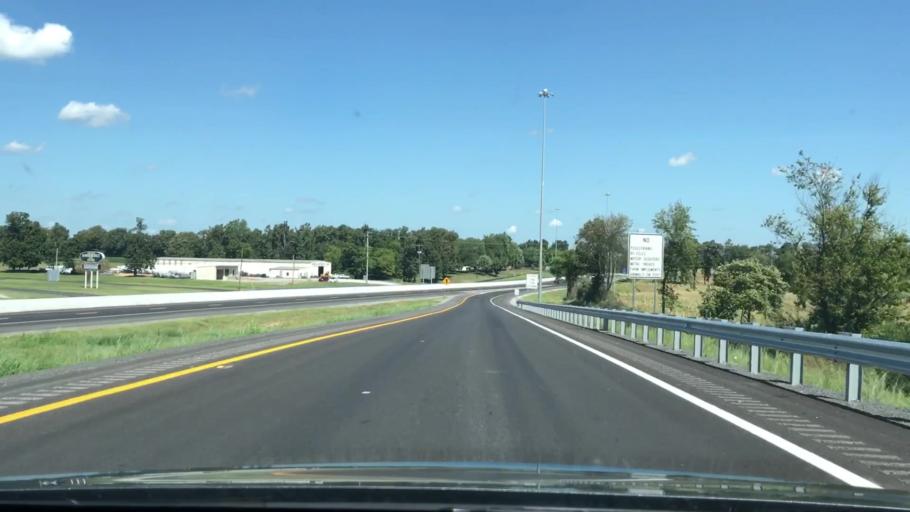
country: US
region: Kentucky
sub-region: Graves County
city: Mayfield
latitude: 36.7399
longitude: -88.6668
